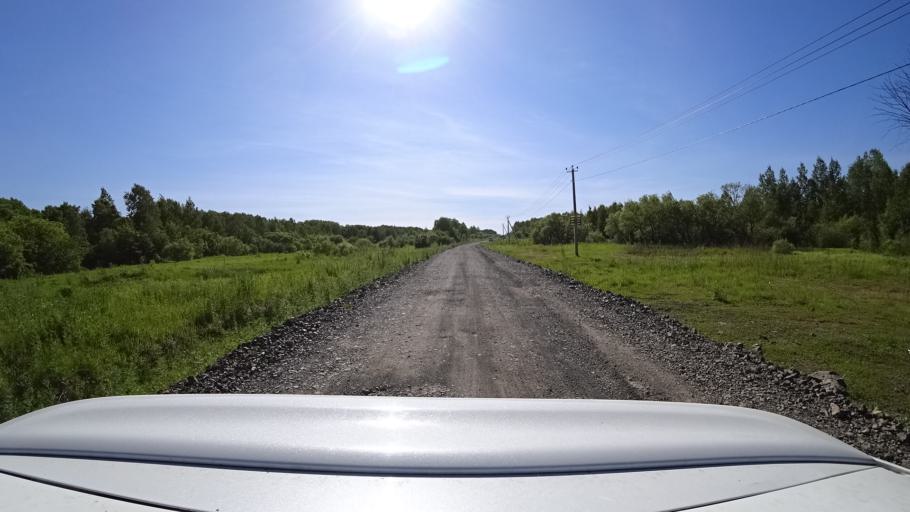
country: RU
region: Khabarovsk Krai
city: Topolevo
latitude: 48.5528
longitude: 135.1850
